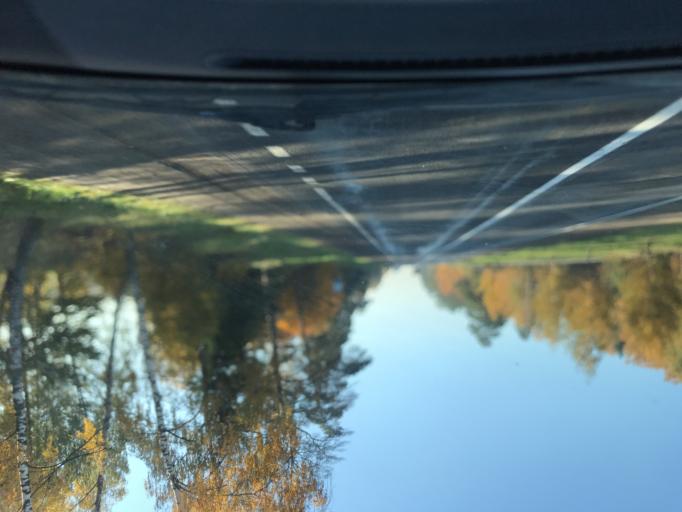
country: BY
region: Brest
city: Lyakhavichy
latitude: 52.9610
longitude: 26.4194
